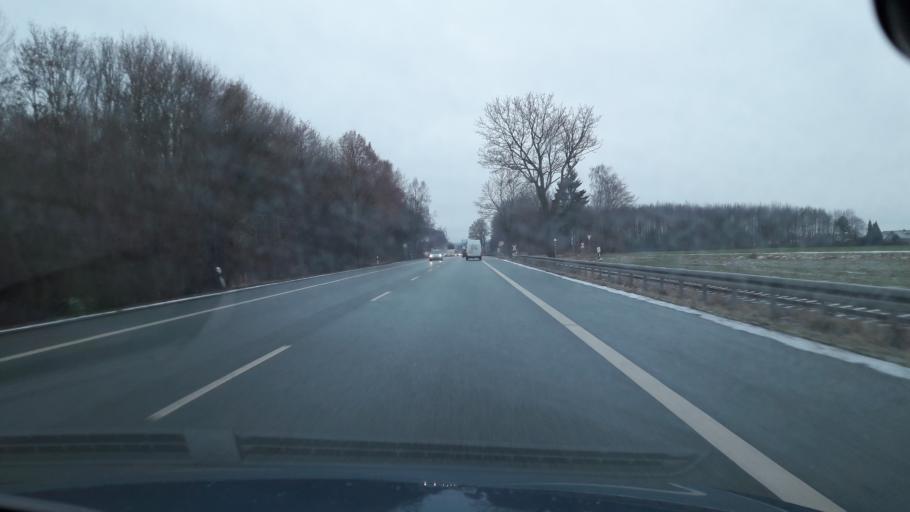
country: DE
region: North Rhine-Westphalia
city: Erwitte
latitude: 51.6220
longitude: 8.3375
